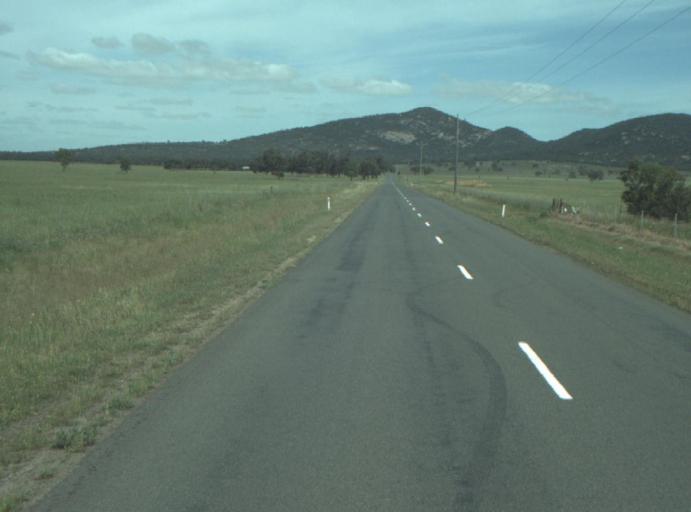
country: AU
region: Victoria
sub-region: Wyndham
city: Little River
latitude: -37.9584
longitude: 144.4754
